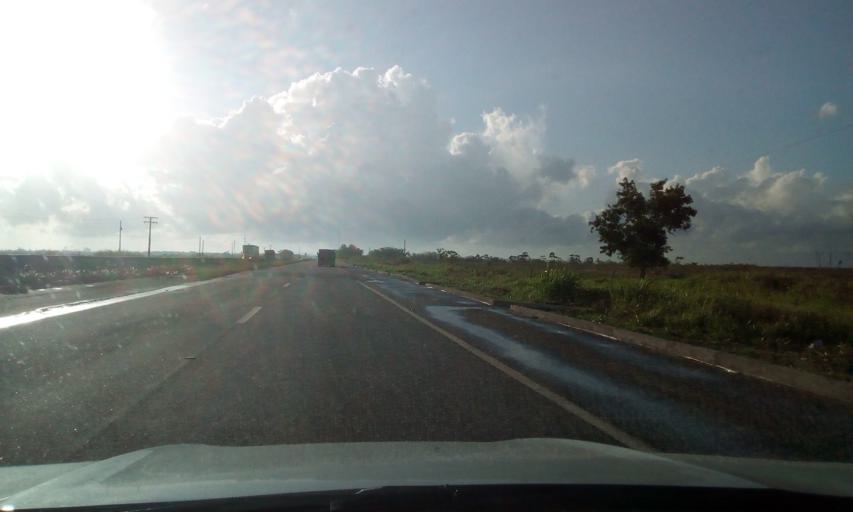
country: BR
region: Pernambuco
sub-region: Goiana
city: Goiana
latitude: -7.6501
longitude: -34.9484
